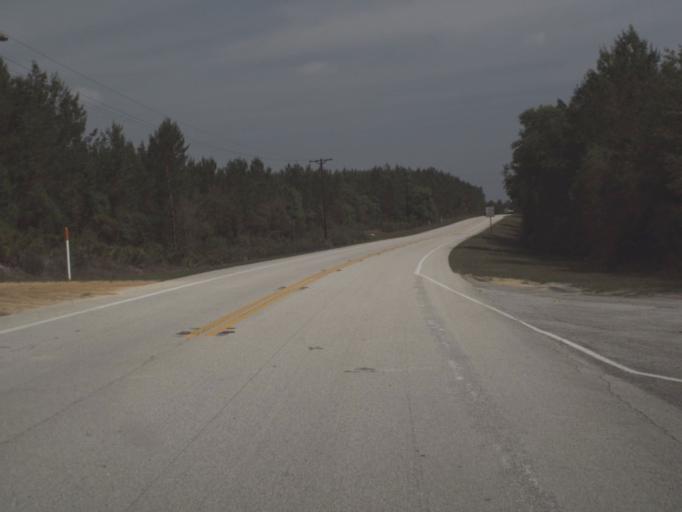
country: US
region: Florida
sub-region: Lake County
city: Astor
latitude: 29.2445
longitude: -81.6479
